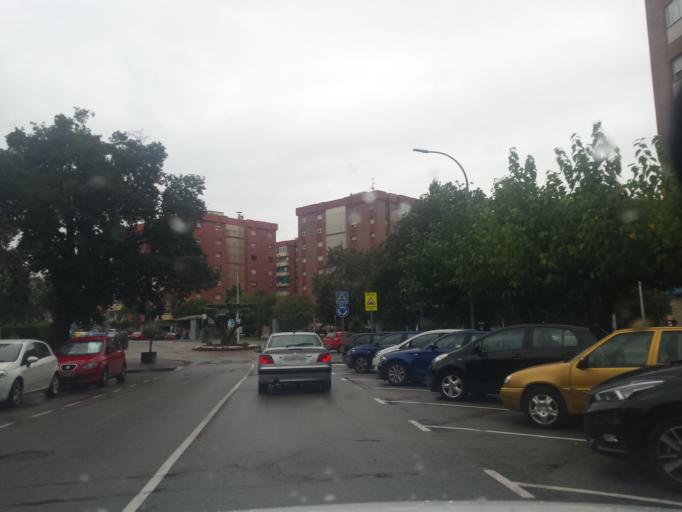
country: ES
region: Catalonia
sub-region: Provincia de Barcelona
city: Sant Andreu de la Barca
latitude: 41.4536
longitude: 1.9601
